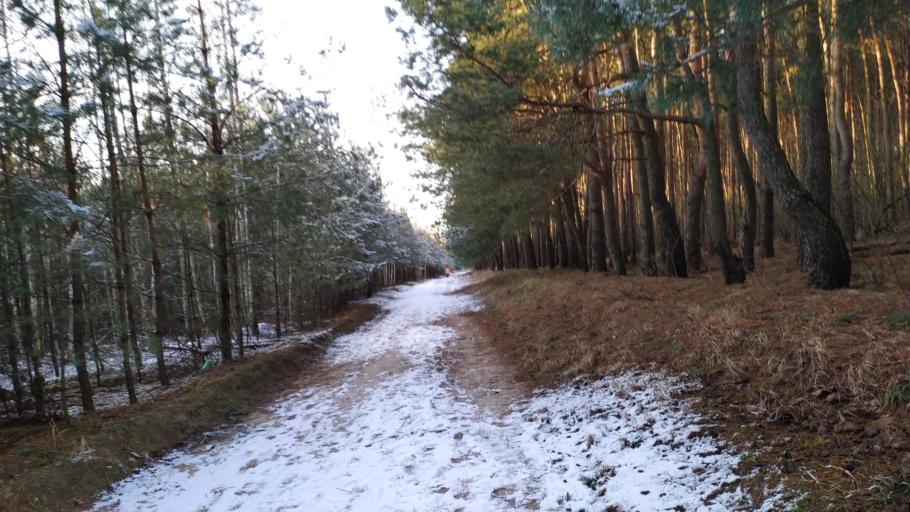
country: BY
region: Brest
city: Kamyanyets
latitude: 52.3827
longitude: 23.8335
